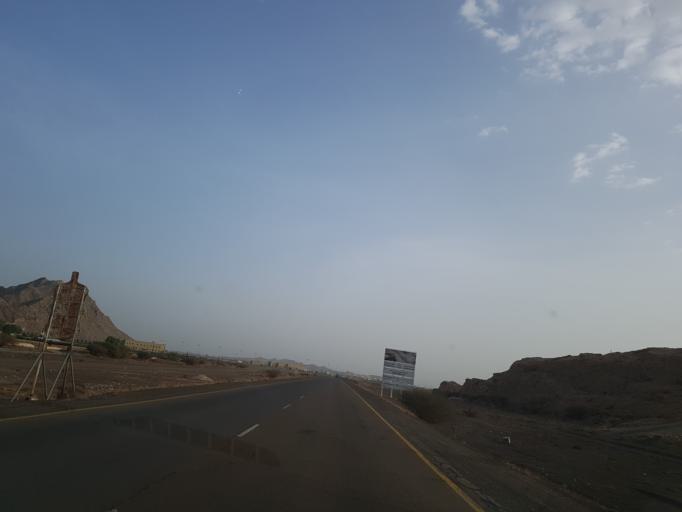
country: OM
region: Al Buraimi
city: Al Buraymi
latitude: 24.2253
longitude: 55.9568
